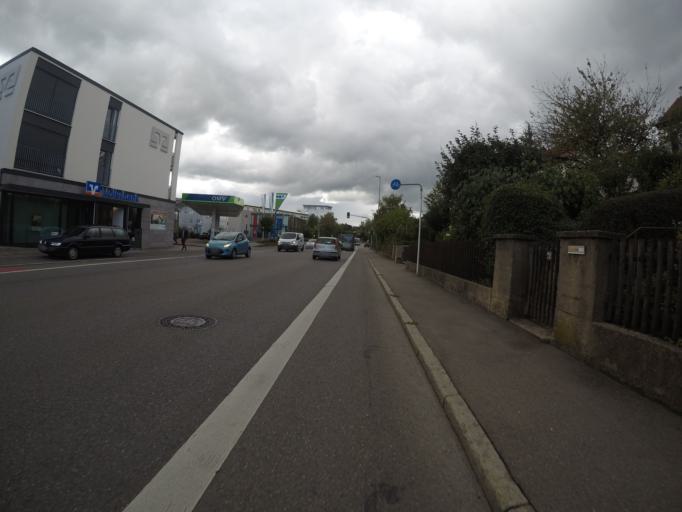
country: DE
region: Baden-Wuerttemberg
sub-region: Tuebingen Region
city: Reutlingen
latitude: 48.4833
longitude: 9.2011
